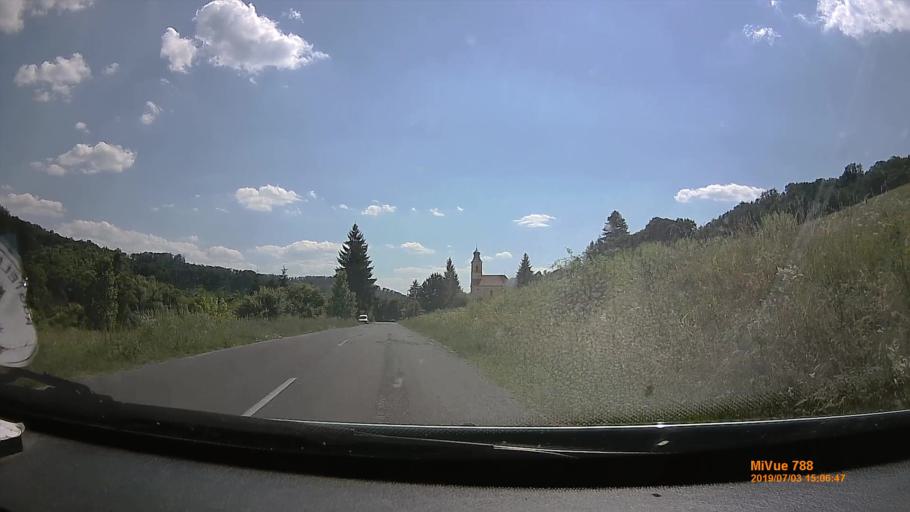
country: HU
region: Borsod-Abauj-Zemplen
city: Putnok
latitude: 48.2566
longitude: 20.3945
